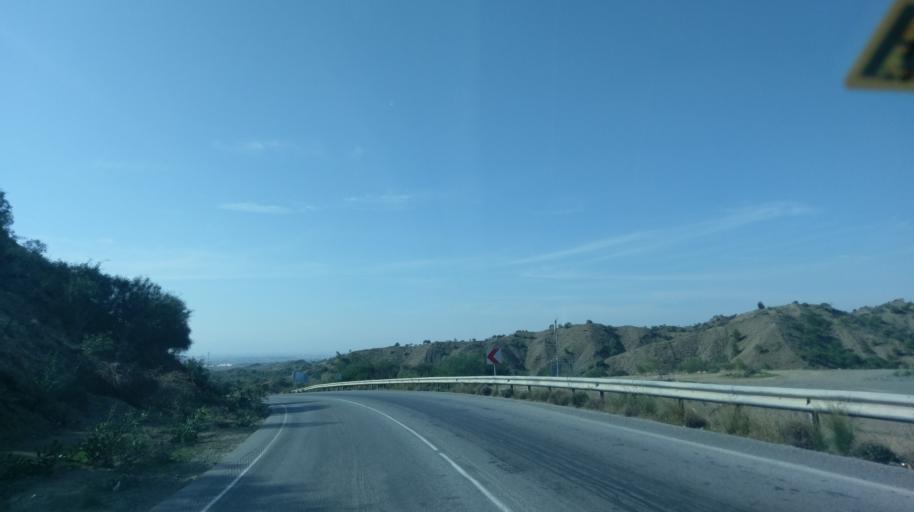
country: CY
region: Lefkosia
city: Nicosia
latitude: 35.2487
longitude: 33.4604
